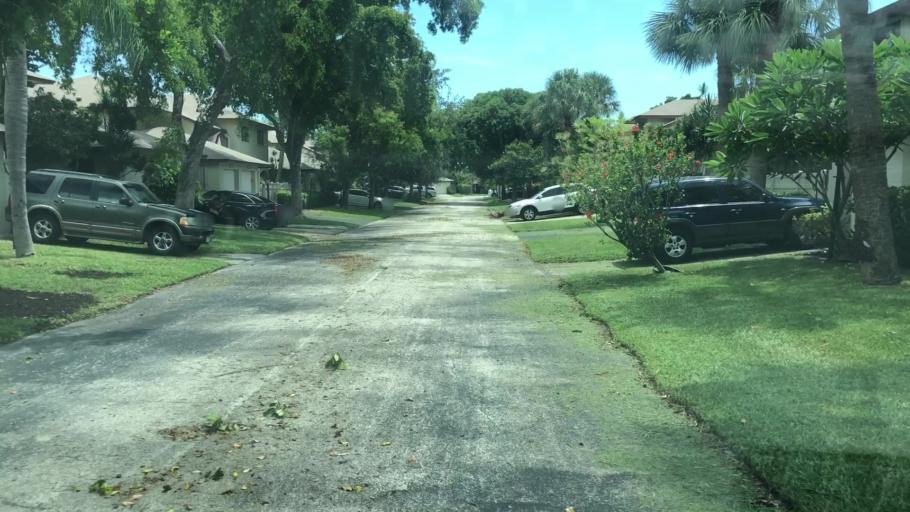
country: US
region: Florida
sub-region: Broward County
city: Pompano Beach Highlands
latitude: 26.2795
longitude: -80.0996
